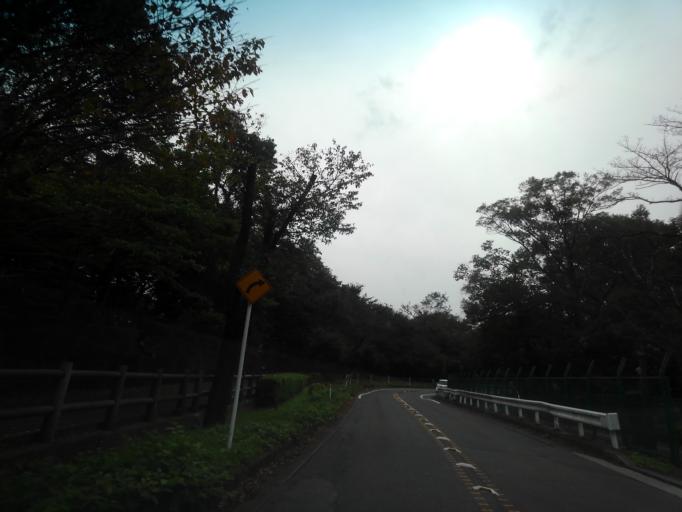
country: JP
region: Tokyo
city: Higashimurayama-shi
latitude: 35.7668
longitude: 139.4205
